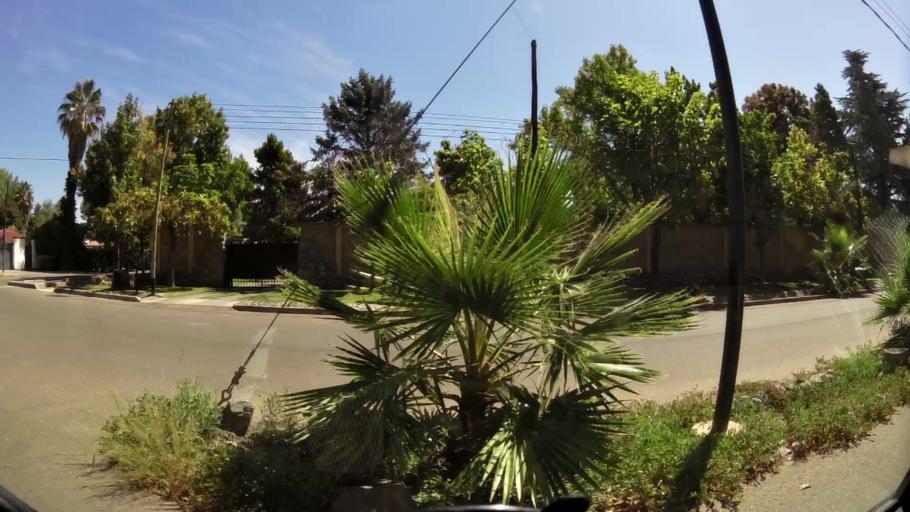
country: AR
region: Mendoza
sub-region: Departamento de Godoy Cruz
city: Godoy Cruz
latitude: -32.9673
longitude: -68.8691
